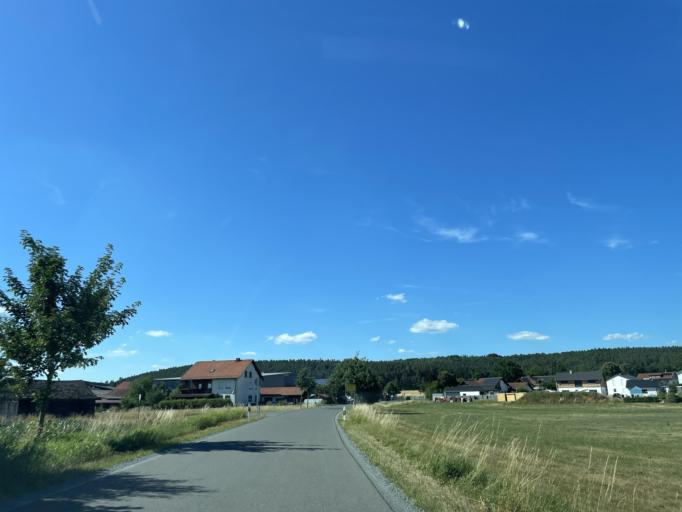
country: DE
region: Bavaria
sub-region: Upper Palatinate
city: Speinshart
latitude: 49.7724
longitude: 11.8606
